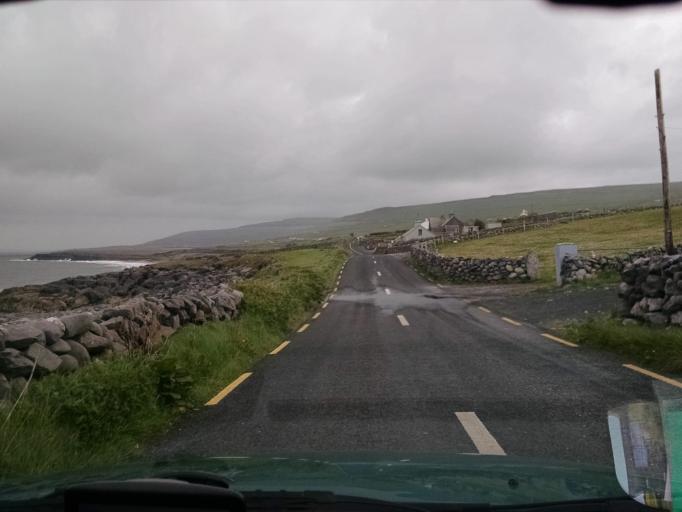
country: IE
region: Connaught
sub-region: County Galway
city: Bearna
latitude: 53.0881
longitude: -9.3156
